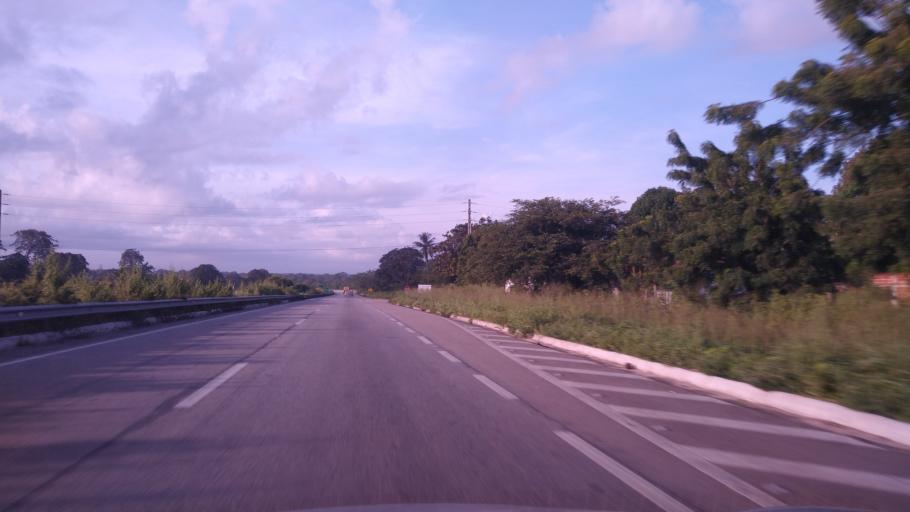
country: BR
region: Ceara
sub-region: Pacajus
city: Pacajus
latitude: -4.1767
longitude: -38.4924
